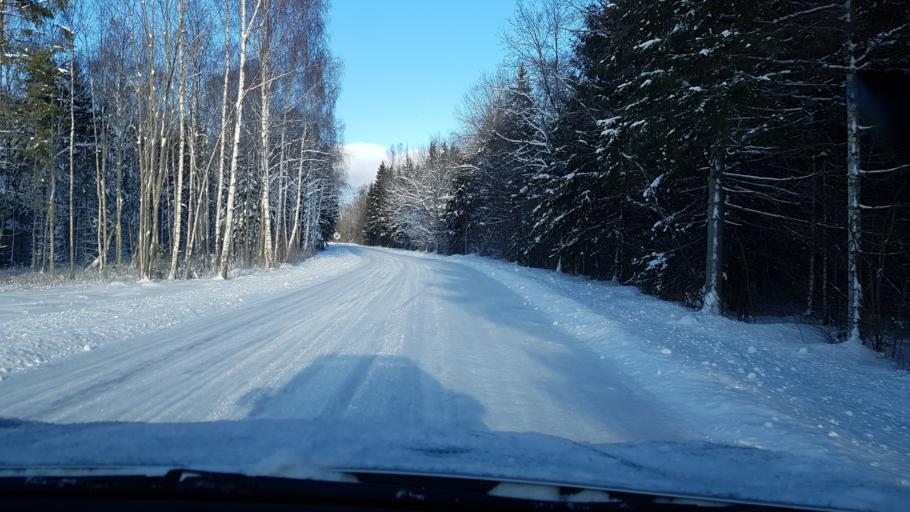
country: EE
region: Harju
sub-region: Nissi vald
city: Turba
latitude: 59.1145
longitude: 24.2214
